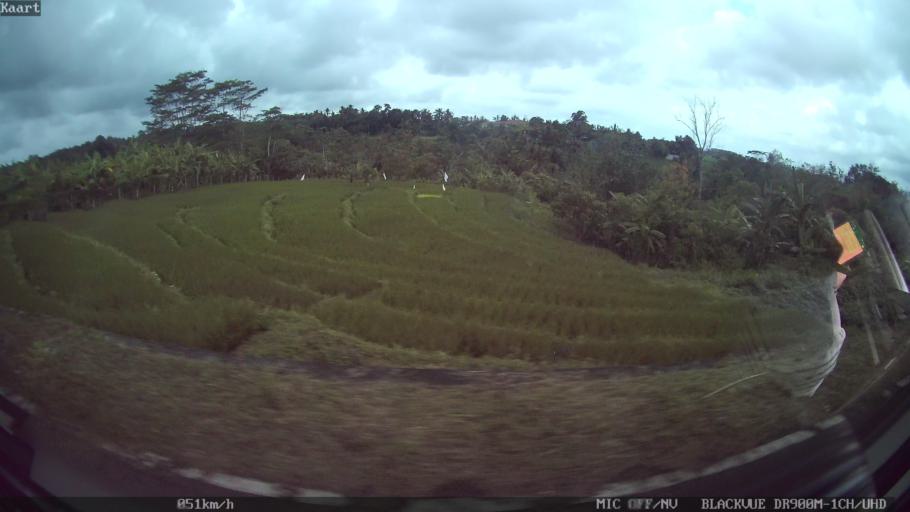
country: ID
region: Bali
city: Banjar Cemenggon
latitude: -8.5362
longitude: 115.1881
